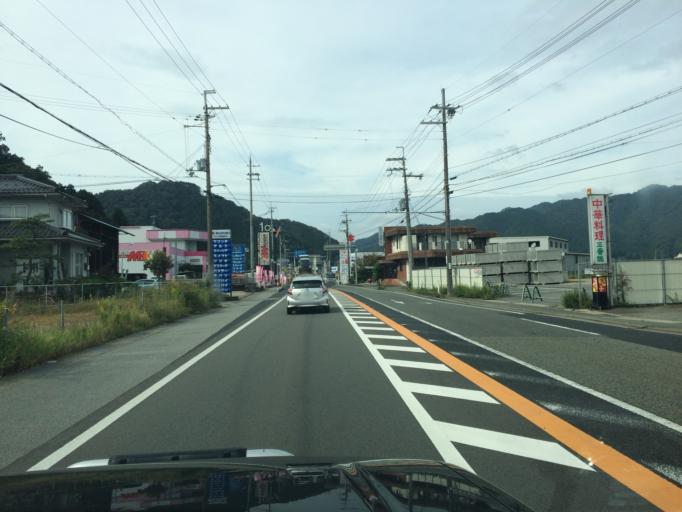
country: JP
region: Hyogo
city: Toyooka
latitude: 35.3440
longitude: 134.8405
